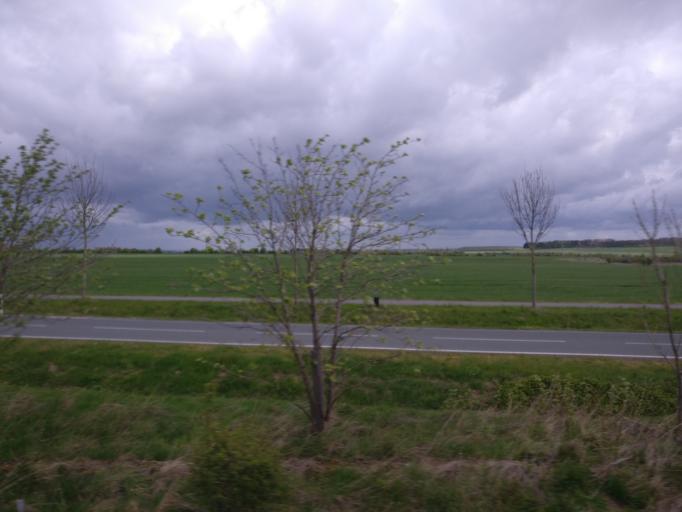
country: DE
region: Saxony-Anhalt
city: Darlingerode
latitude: 51.8467
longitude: 10.7440
